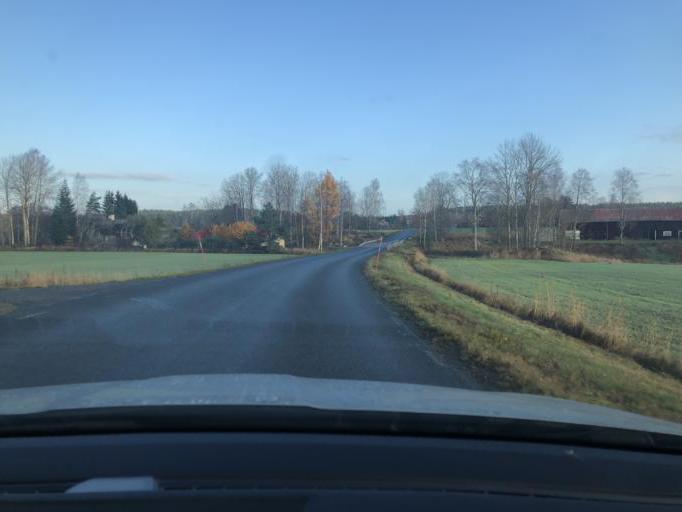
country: SE
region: Soedermanland
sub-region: Flens Kommun
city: Halleforsnas
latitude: 59.0549
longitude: 16.3787
